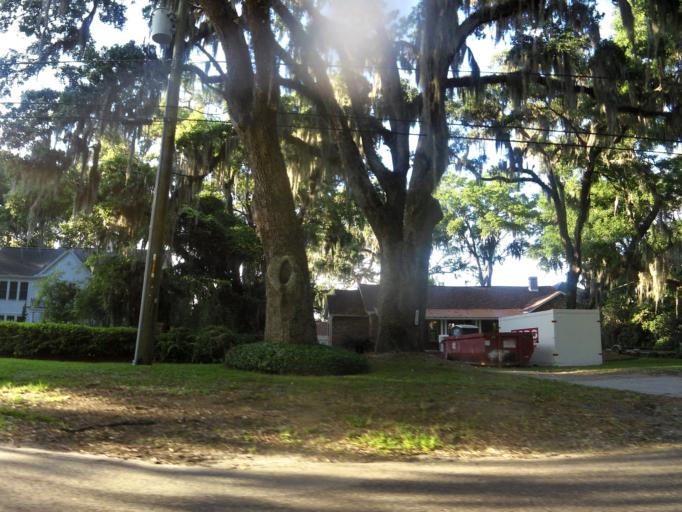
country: US
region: Florida
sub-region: Duval County
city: Jacksonville
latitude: 30.2729
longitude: -81.7097
